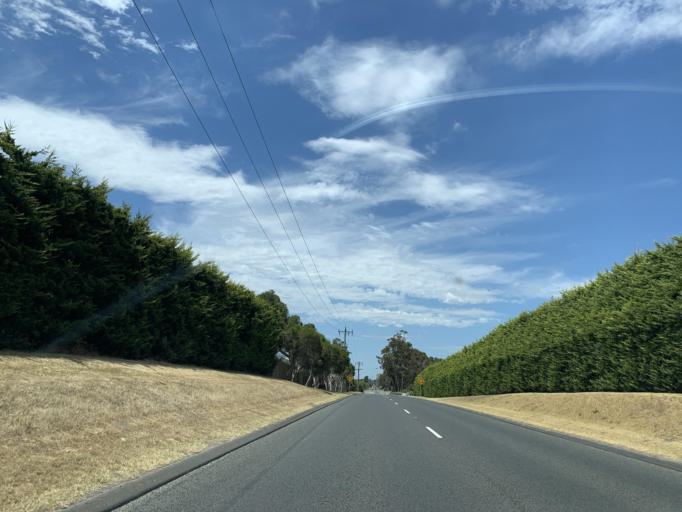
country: AU
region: Victoria
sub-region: Mornington Peninsula
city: Tyabb
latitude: -38.2386
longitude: 145.2106
